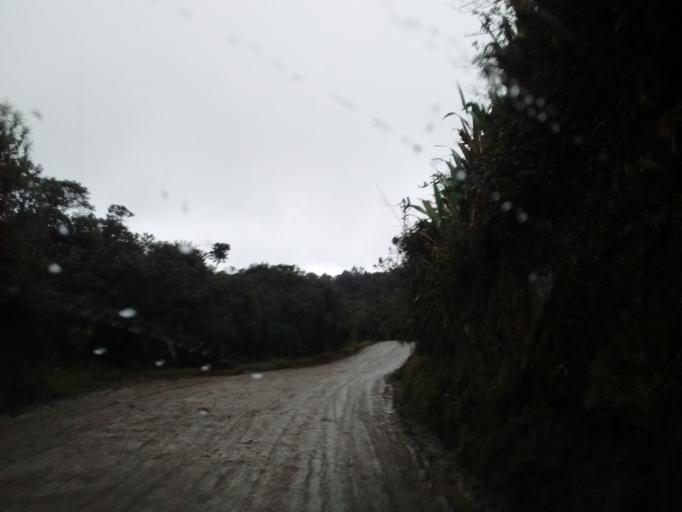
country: CO
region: Cauca
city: Paispamba
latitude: 2.1650
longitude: -76.4030
